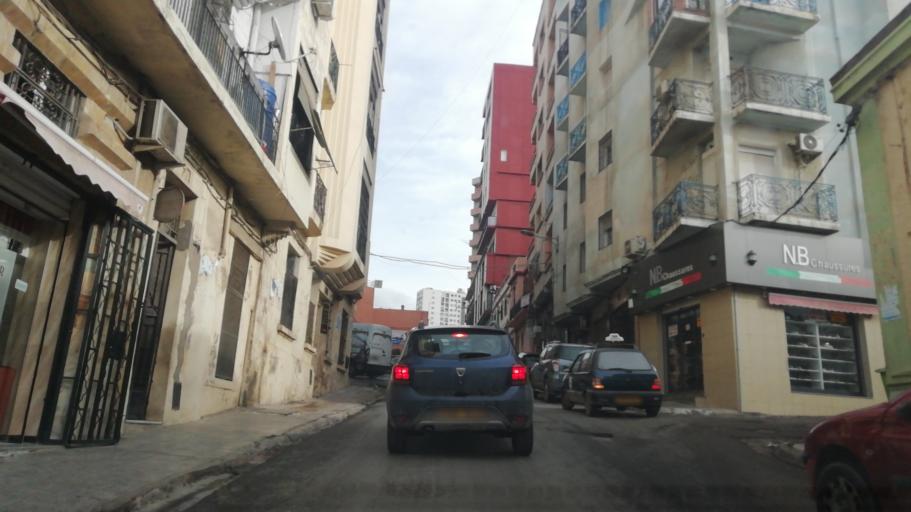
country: DZ
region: Oran
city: Oran
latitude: 35.7023
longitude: -0.6327
